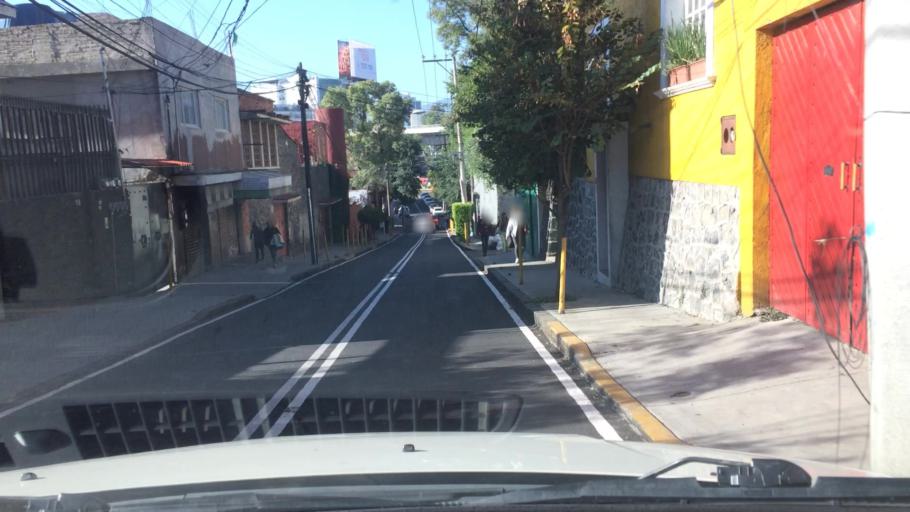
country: MX
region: Mexico City
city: Magdalena Contreras
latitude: 19.3247
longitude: -99.2236
